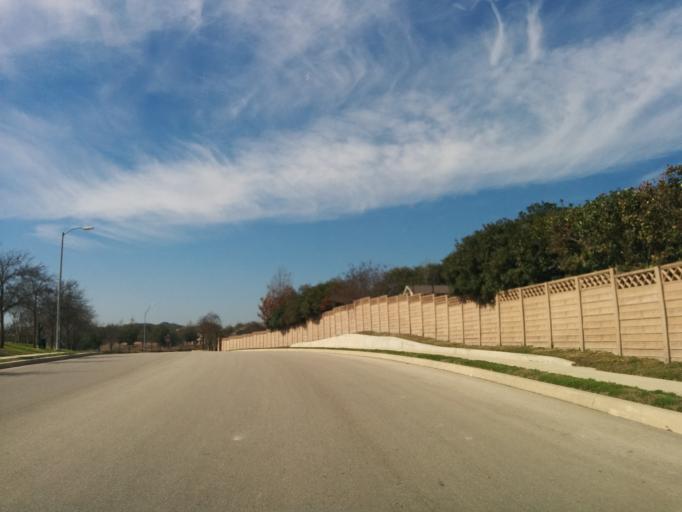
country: US
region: Texas
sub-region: Bexar County
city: Cross Mountain
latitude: 29.6678
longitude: -98.6368
